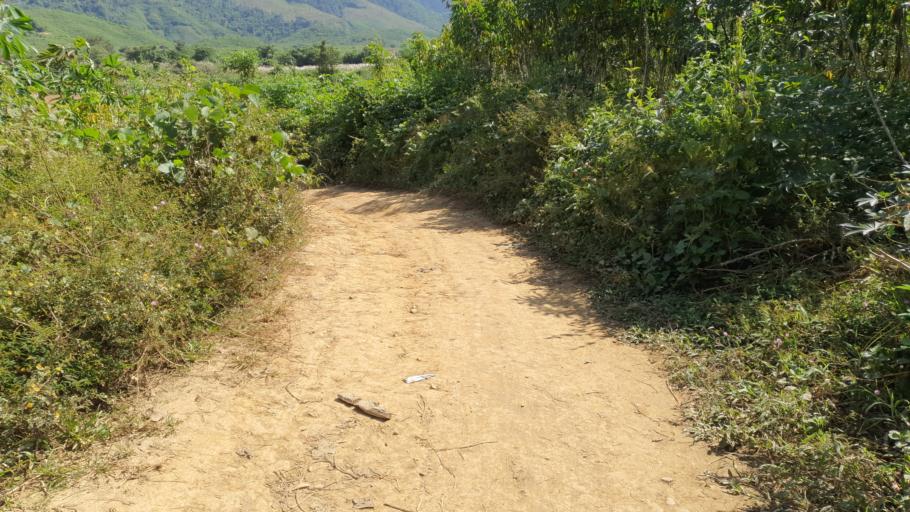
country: LA
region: Bolikhamxai
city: Bolikhan
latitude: 18.9062
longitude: 103.7419
